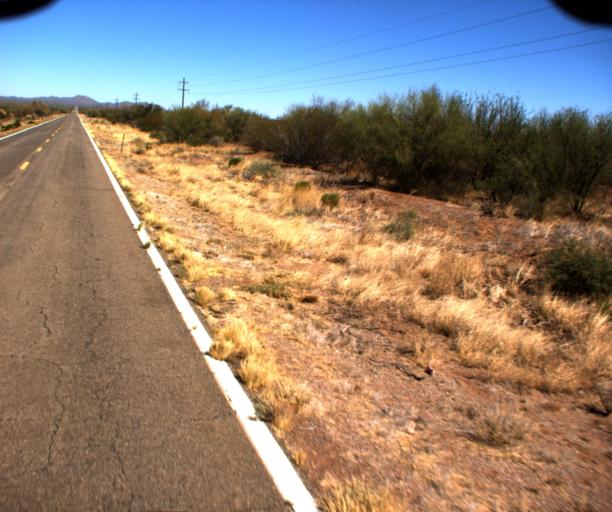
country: US
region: Arizona
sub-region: Pima County
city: Sells
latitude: 32.0765
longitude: -112.0466
